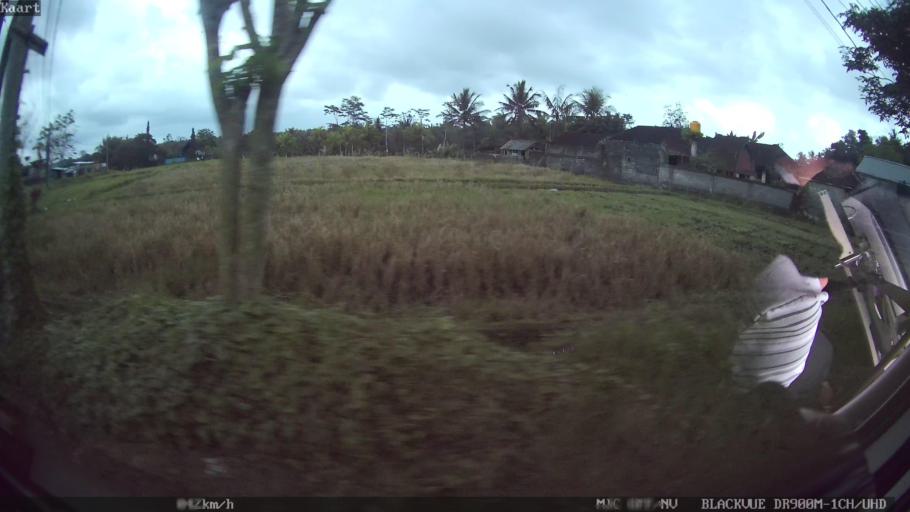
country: ID
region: Bali
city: Banjar Sempidi
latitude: -8.5238
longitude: 115.1998
